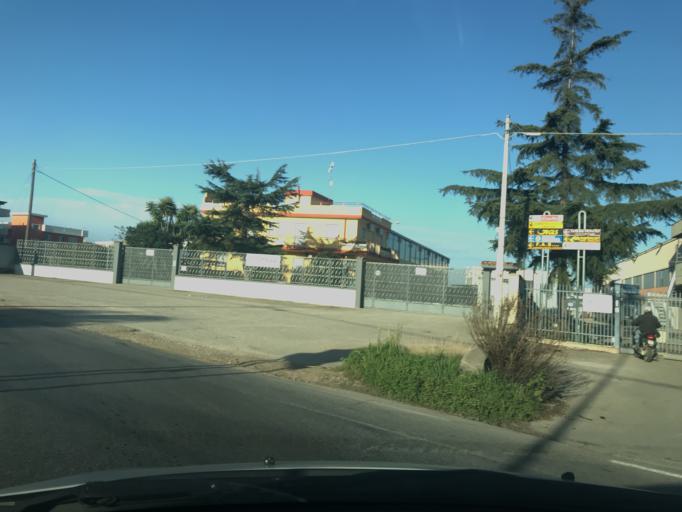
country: IT
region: Apulia
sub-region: Provincia di Bari
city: Corato
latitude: 41.1348
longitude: 16.4137
